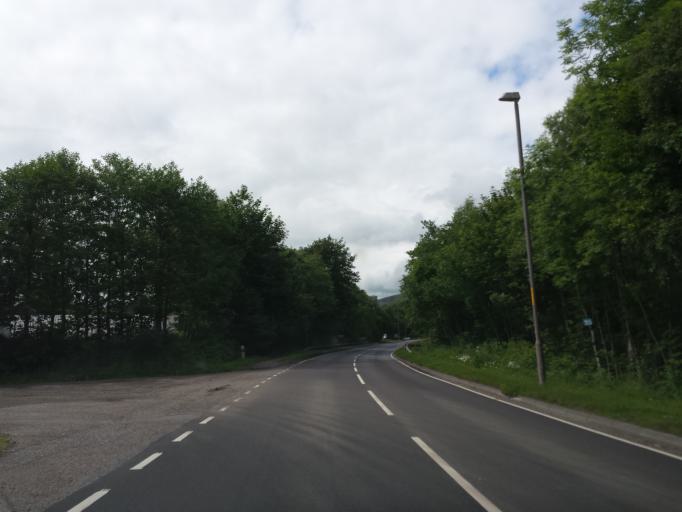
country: GB
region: Scotland
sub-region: Highland
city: Fort William
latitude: 56.8436
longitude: -5.1485
